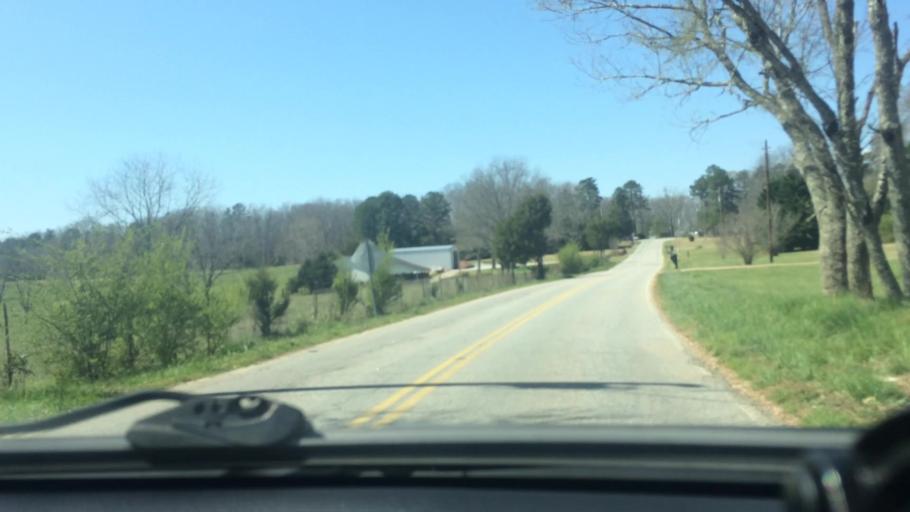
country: US
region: South Carolina
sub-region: Anderson County
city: Powdersville
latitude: 34.7889
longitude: -82.5009
